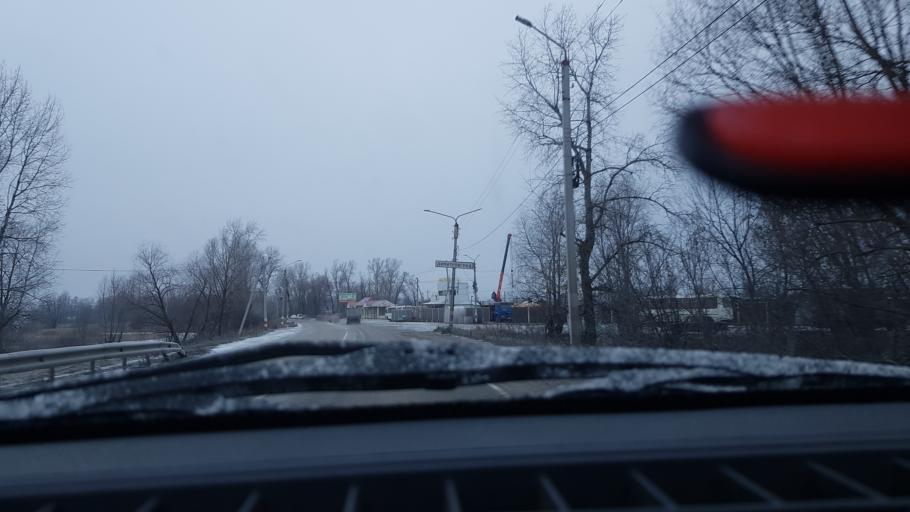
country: RU
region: Ulyanovsk
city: Dimitrovgrad
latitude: 54.1860
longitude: 49.6546
